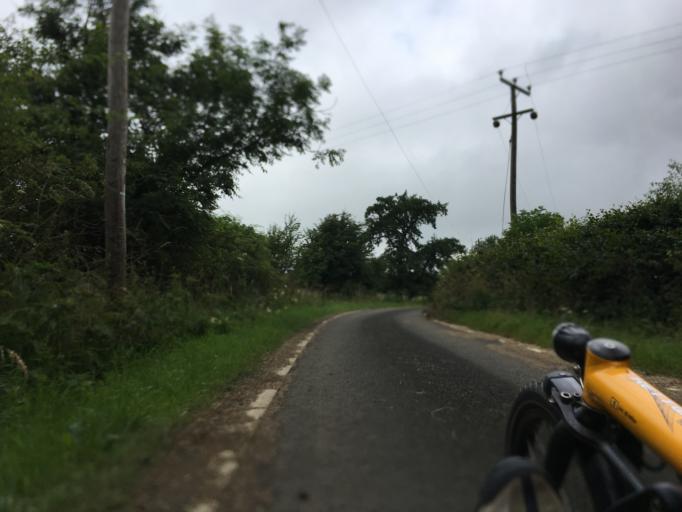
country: GB
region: Scotland
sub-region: West Lothian
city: West Calder
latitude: 55.8474
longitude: -3.5329
